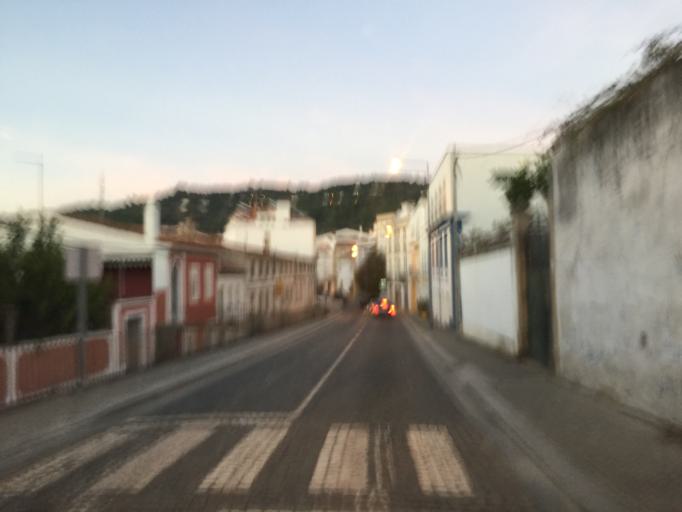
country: PT
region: Portalegre
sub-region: Portalegre
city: Portalegre
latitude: 39.2938
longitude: -7.4323
